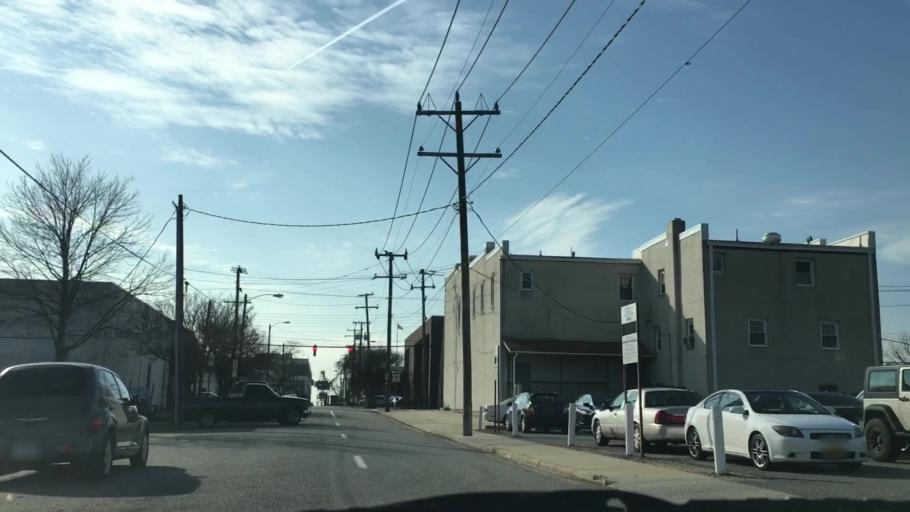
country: US
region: Virginia
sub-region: City of Newport News
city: Newport News
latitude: 36.9865
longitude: -76.4326
